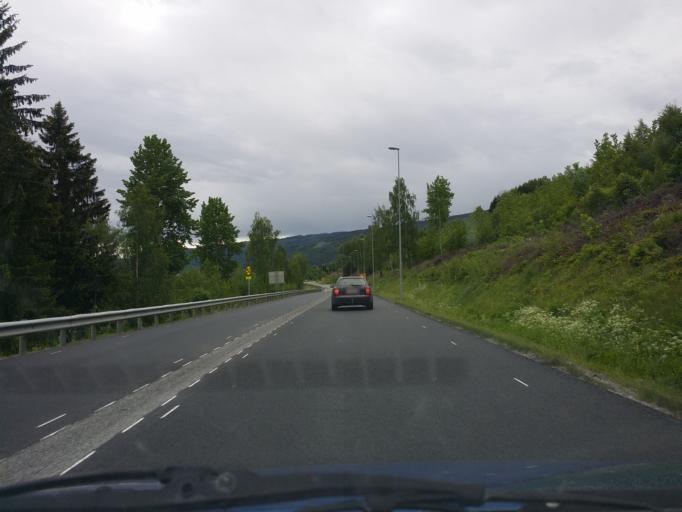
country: NO
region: Oppland
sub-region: Lillehammer
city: Lillehammer
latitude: 61.0541
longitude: 10.4344
